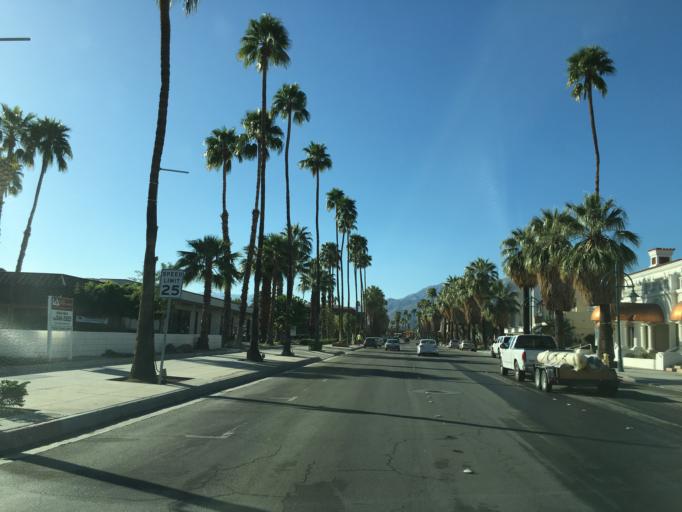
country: US
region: California
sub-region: Riverside County
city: Palm Springs
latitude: 33.8188
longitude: -116.5468
